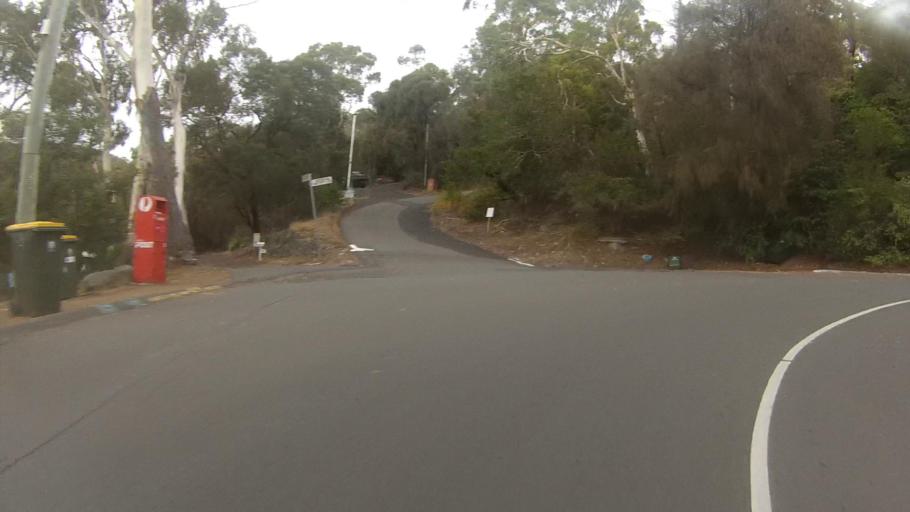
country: AU
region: Tasmania
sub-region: Hobart
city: Dynnyrne
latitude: -42.9111
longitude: 147.3279
